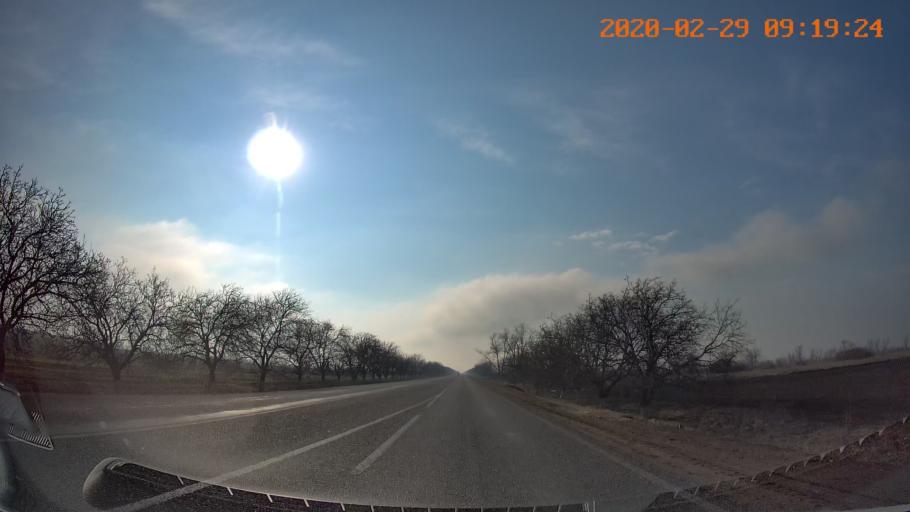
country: MD
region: Telenesti
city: Pervomaisc
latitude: 46.7632
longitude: 29.9387
